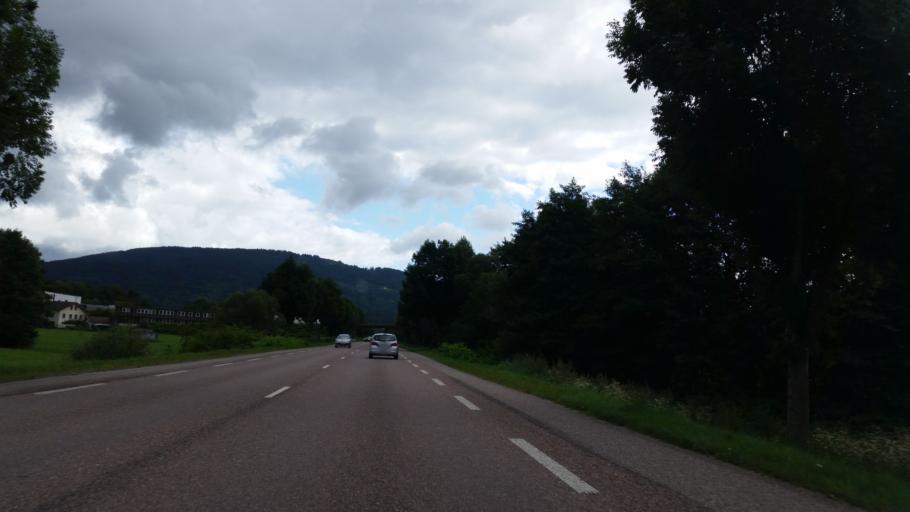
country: FR
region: Lorraine
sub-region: Departement des Vosges
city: Saint-Ame
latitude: 48.0164
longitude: 6.6643
